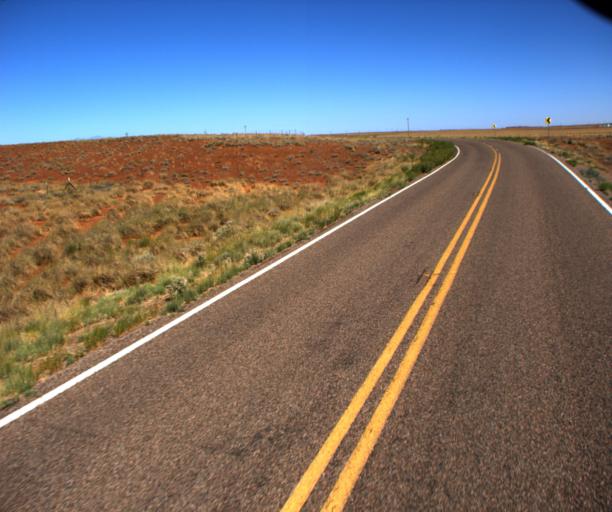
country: US
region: Arizona
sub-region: Coconino County
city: LeChee
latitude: 35.1722
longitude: -110.9186
